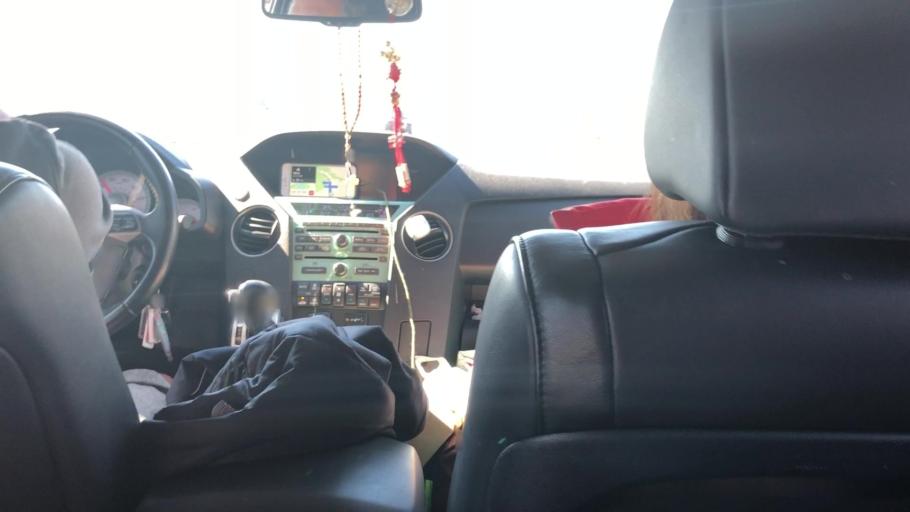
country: US
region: Louisiana
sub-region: Saint John the Baptist Parish
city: Montegut
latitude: 30.1036
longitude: -90.5021
